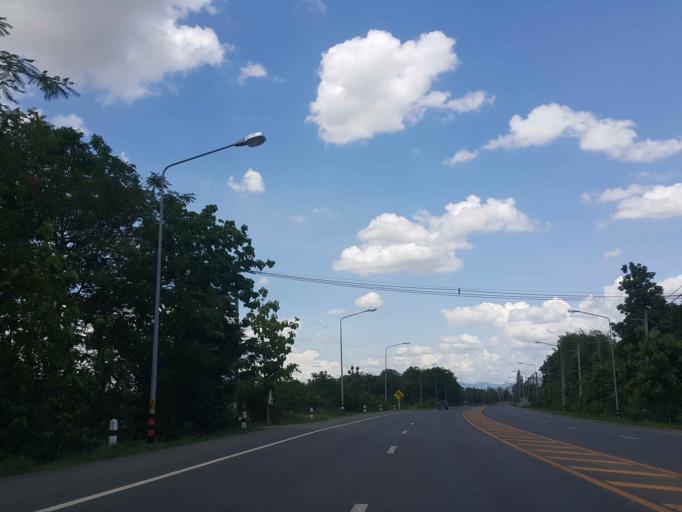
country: TH
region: Phrae
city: Nong Muang Khai
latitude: 18.2042
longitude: 100.2030
